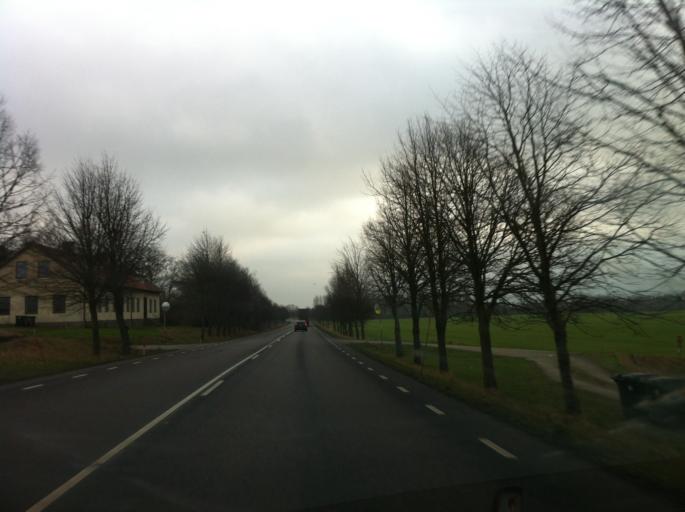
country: SE
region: Skane
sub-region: Eslovs Kommun
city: Eslov
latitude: 55.7762
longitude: 13.3058
